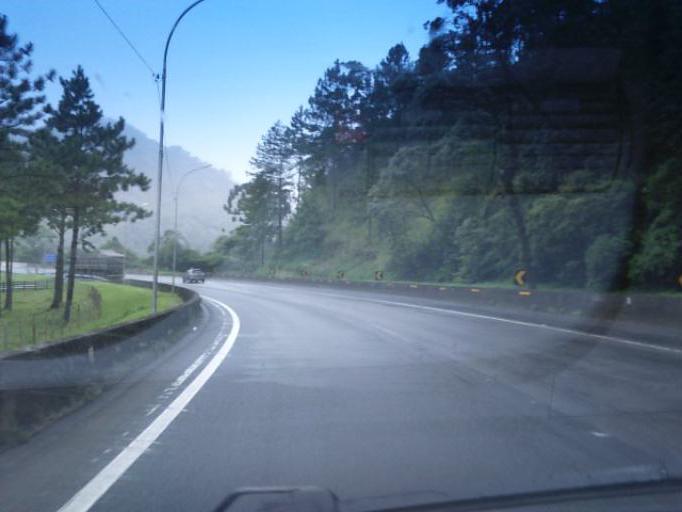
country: BR
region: Parana
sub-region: Campina Grande Do Sul
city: Campina Grande do Sul
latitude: -25.1125
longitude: -48.8045
